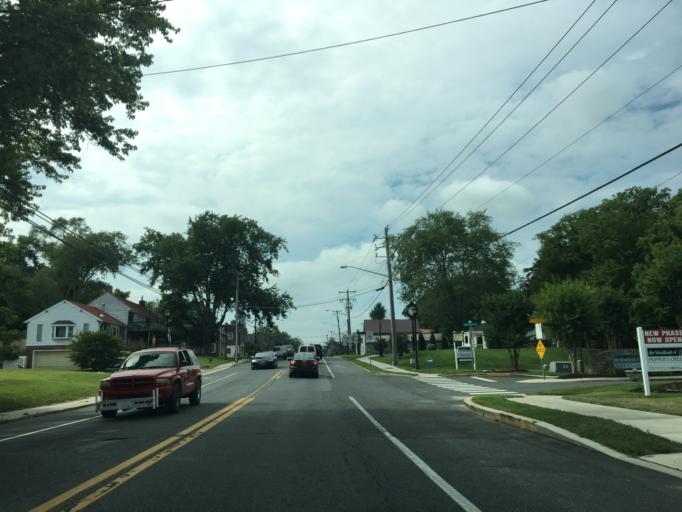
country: US
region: Delaware
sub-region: Sussex County
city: Millsboro
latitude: 38.5473
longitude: -75.2440
